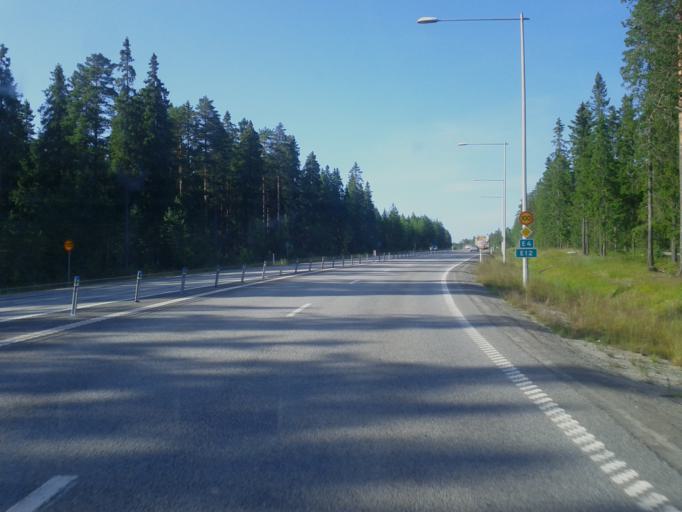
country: SE
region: Vaesterbotten
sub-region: Umea Kommun
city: Ersmark
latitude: 63.8190
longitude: 20.3286
